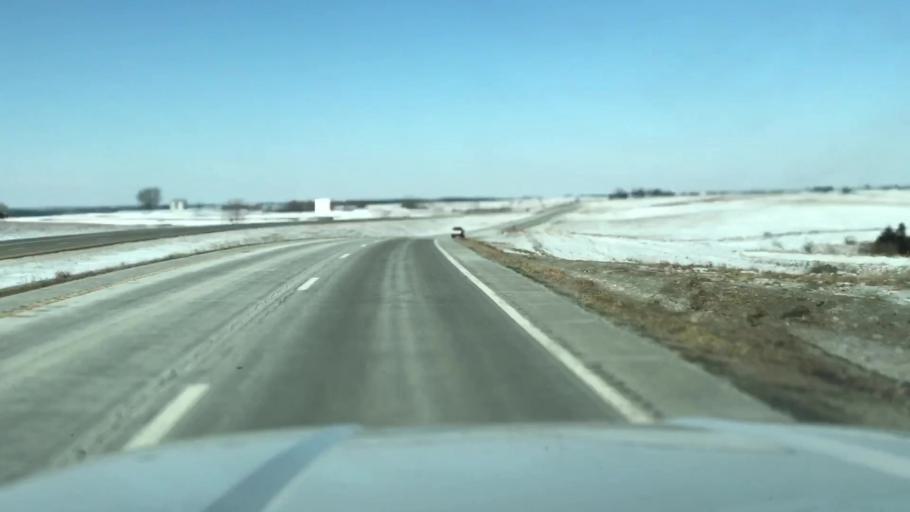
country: US
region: Missouri
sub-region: Andrew County
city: Savannah
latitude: 39.9729
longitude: -94.8739
